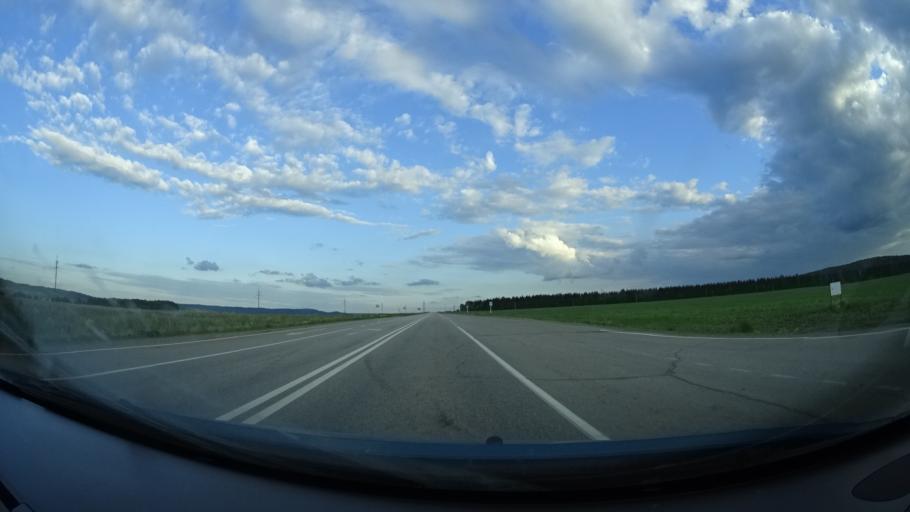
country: RU
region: Perm
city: Barda
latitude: 57.0217
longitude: 55.5555
